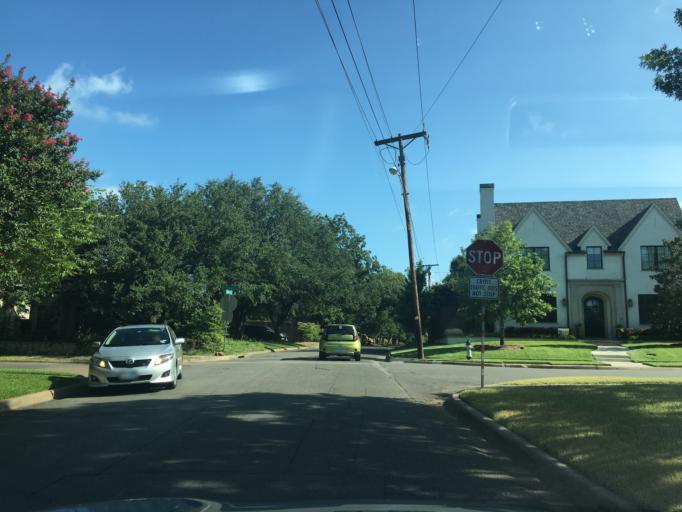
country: US
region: Texas
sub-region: Dallas County
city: Highland Park
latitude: 32.8323
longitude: -96.7500
